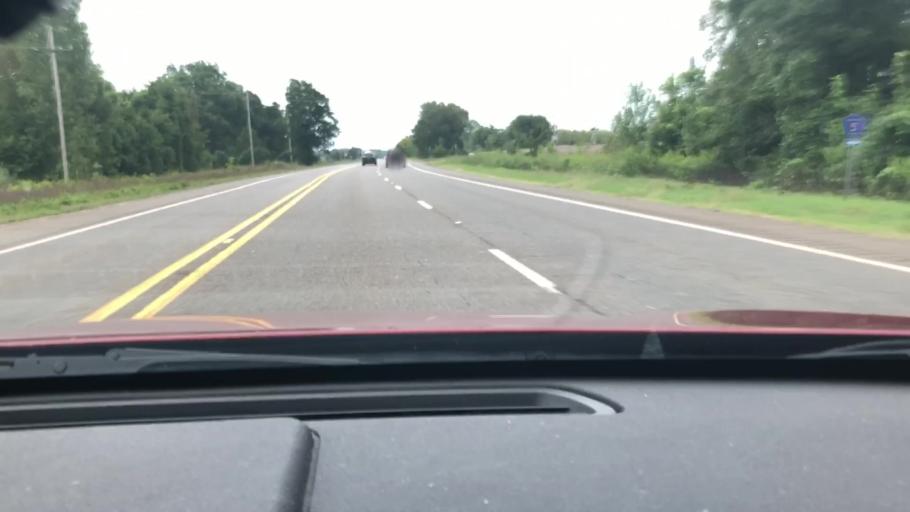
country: US
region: Arkansas
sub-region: Lafayette County
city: Lewisville
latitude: 33.3555
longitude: -93.6618
